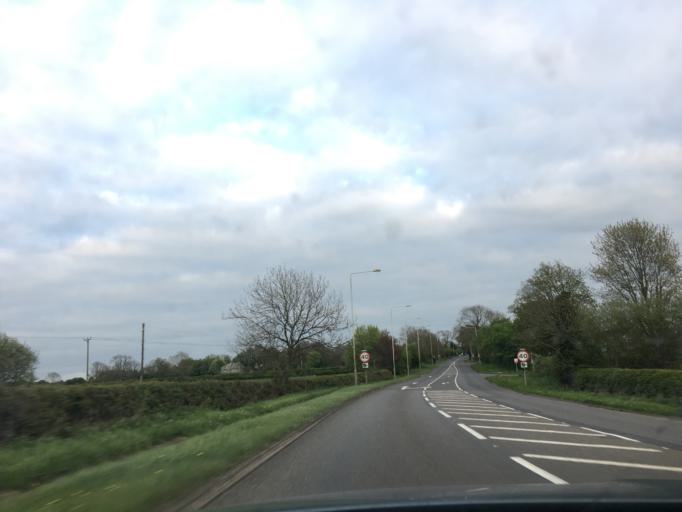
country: GB
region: England
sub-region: Leicestershire
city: Houghton on the Hill
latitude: 52.6297
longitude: -1.0033
